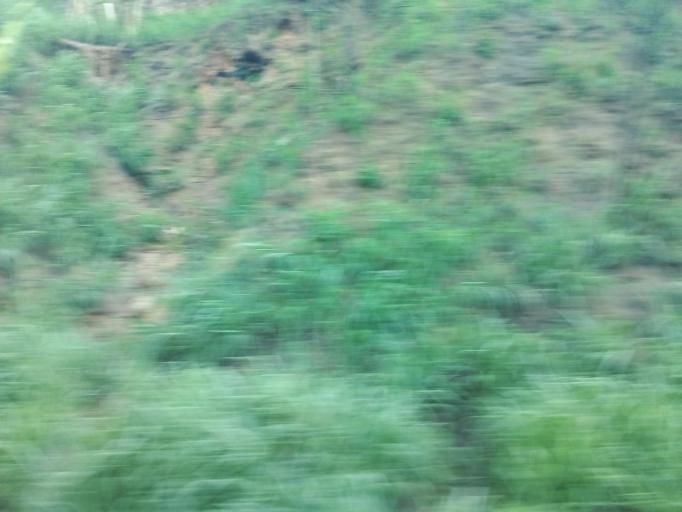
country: BR
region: Minas Gerais
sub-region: Coronel Fabriciano
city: Coronel Fabriciano
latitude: -19.5274
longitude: -42.6690
